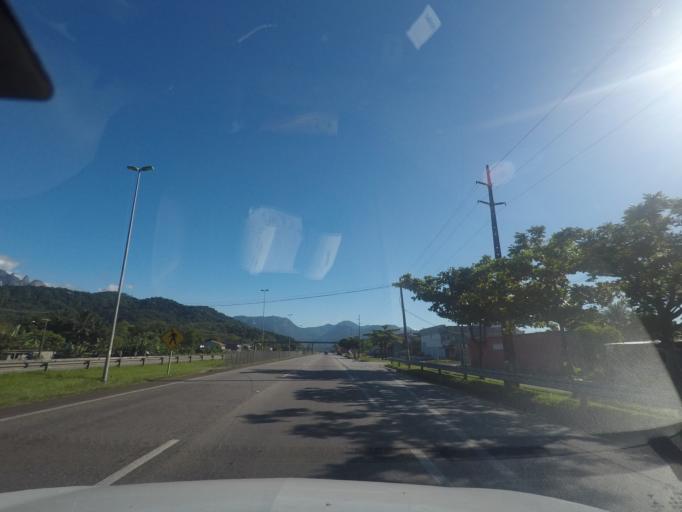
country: BR
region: Rio de Janeiro
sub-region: Guapimirim
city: Guapimirim
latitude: -22.5617
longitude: -42.9973
